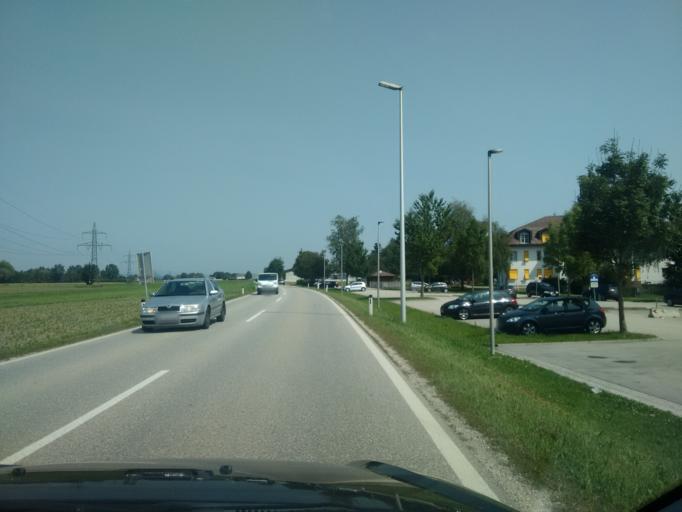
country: AT
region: Upper Austria
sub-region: Wels-Land
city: Gunskirchen
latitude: 48.1347
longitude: 13.9403
